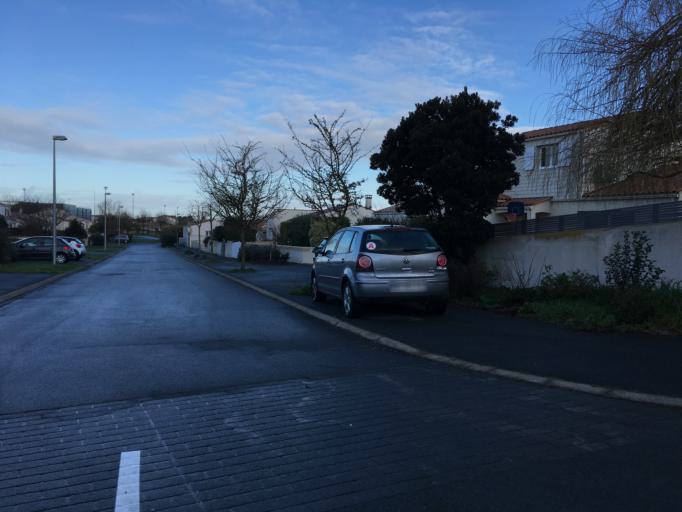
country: FR
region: Poitou-Charentes
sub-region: Departement de la Charente-Maritime
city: Nieul-sur-Mer
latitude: 46.2021
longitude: -1.1720
